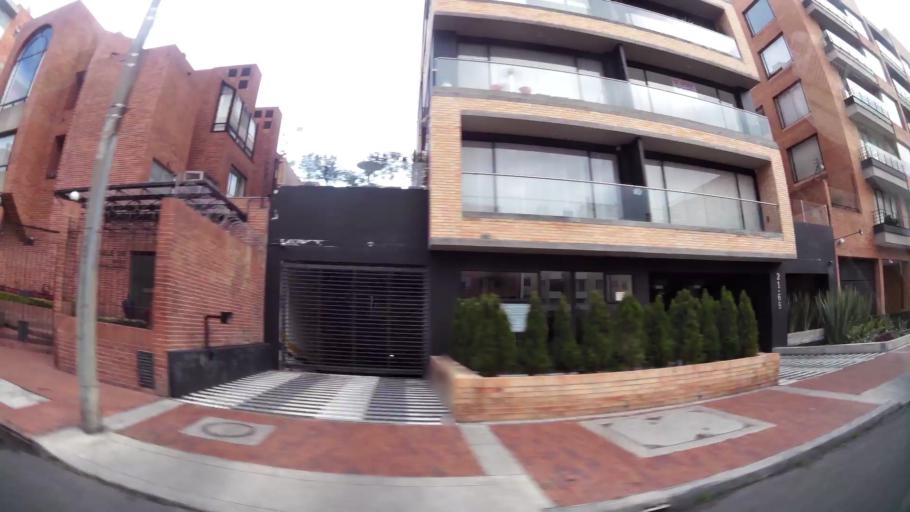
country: CO
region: Bogota D.C.
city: Barrio San Luis
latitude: 4.6926
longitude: -74.0542
